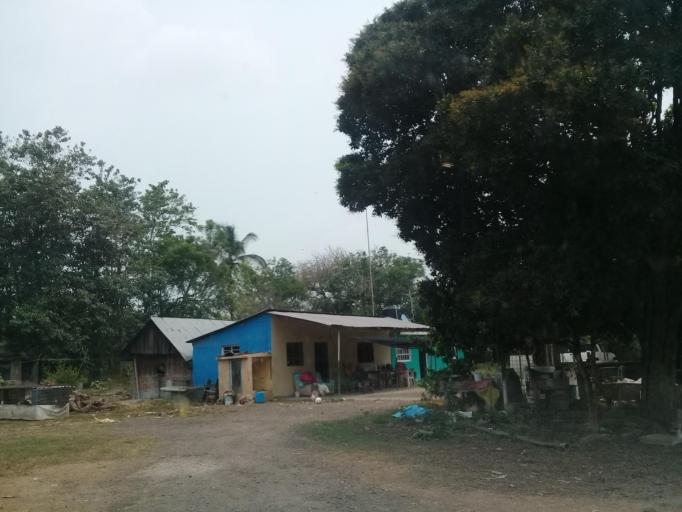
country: MX
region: Veracruz
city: Jamapa
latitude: 18.9561
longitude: -96.1957
